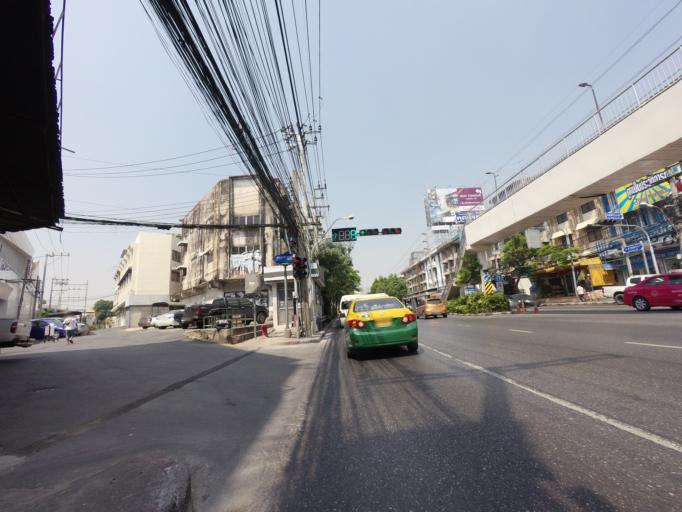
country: TH
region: Bangkok
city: Bang Kapi
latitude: 13.7749
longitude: 100.6291
